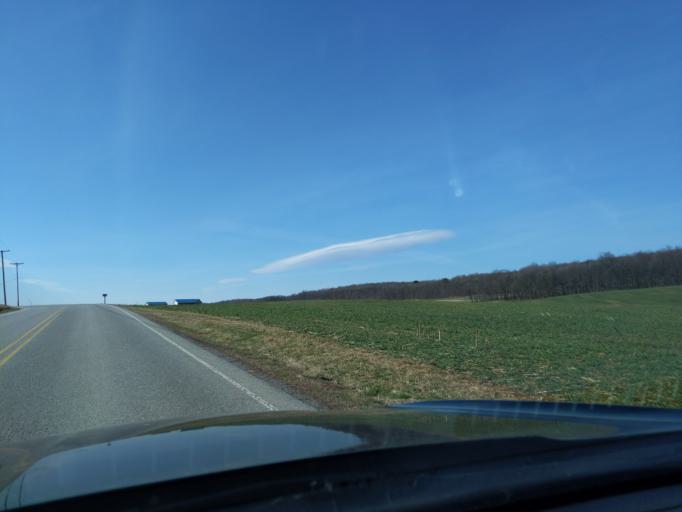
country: US
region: Pennsylvania
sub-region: Blair County
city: Martinsburg
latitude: 40.3585
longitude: -78.2498
